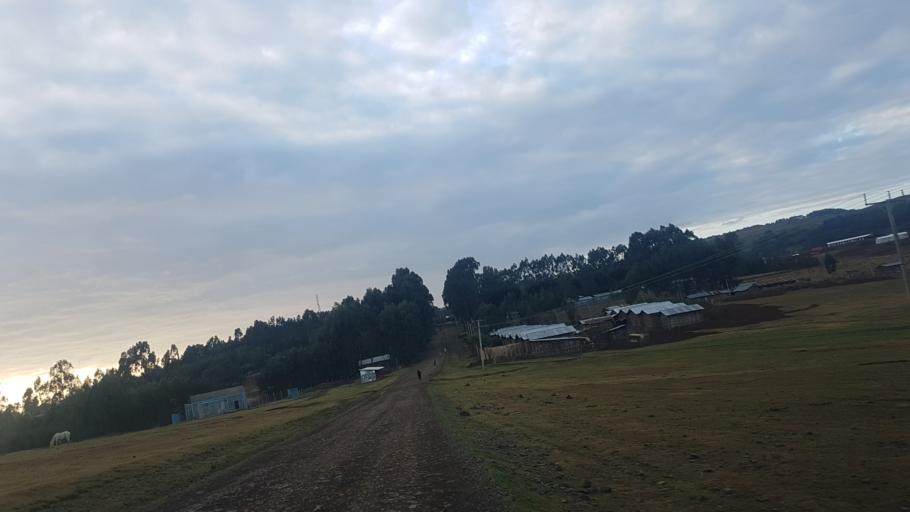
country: ET
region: Amhara
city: Finote Selam
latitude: 10.8156
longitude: 37.6458
